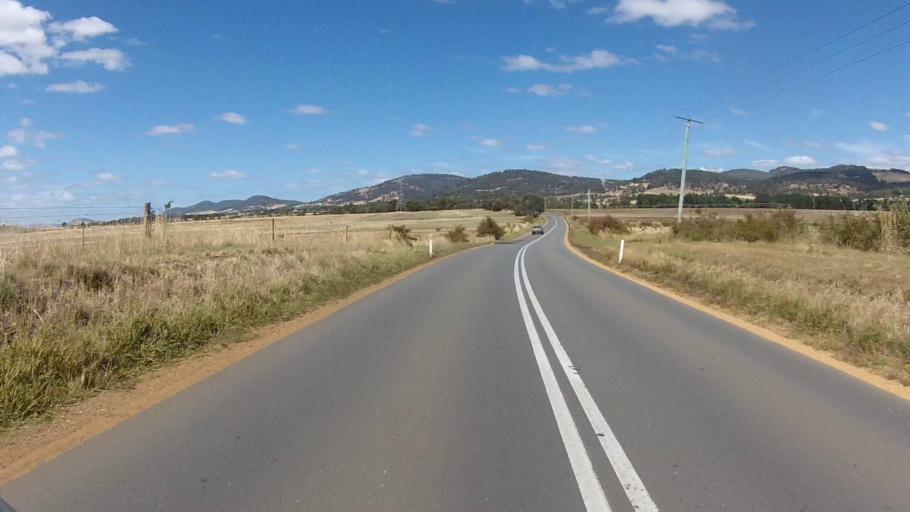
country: AU
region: Tasmania
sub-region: Clarence
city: Cambridge
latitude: -42.7605
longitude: 147.4159
